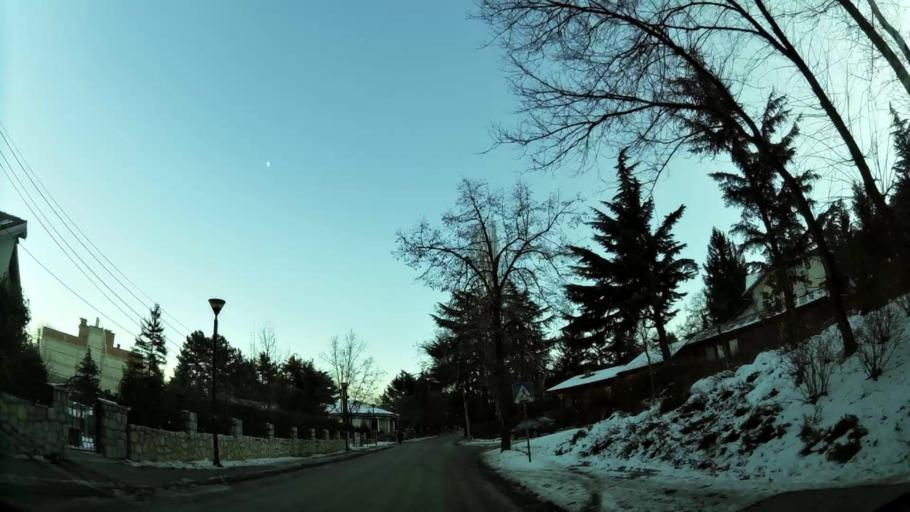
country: MK
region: Karpos
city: Skopje
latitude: 41.9899
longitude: 21.4116
